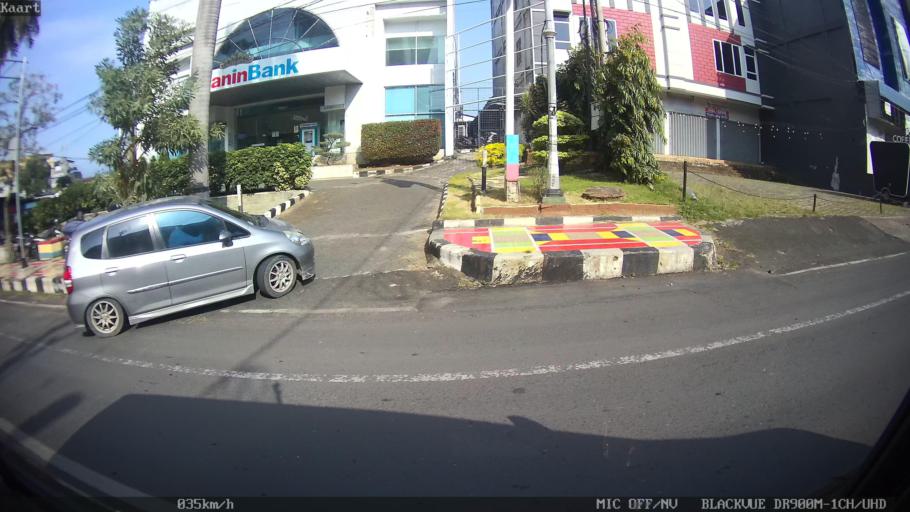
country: ID
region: Lampung
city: Bandarlampung
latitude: -5.4151
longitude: 105.2544
